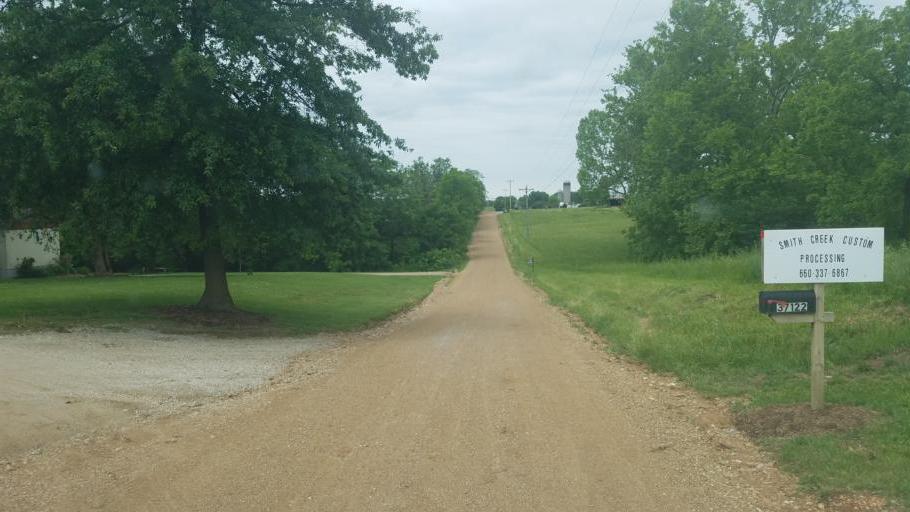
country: US
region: Missouri
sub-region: Moniteau County
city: Tipton
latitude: 38.5345
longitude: -92.7458
